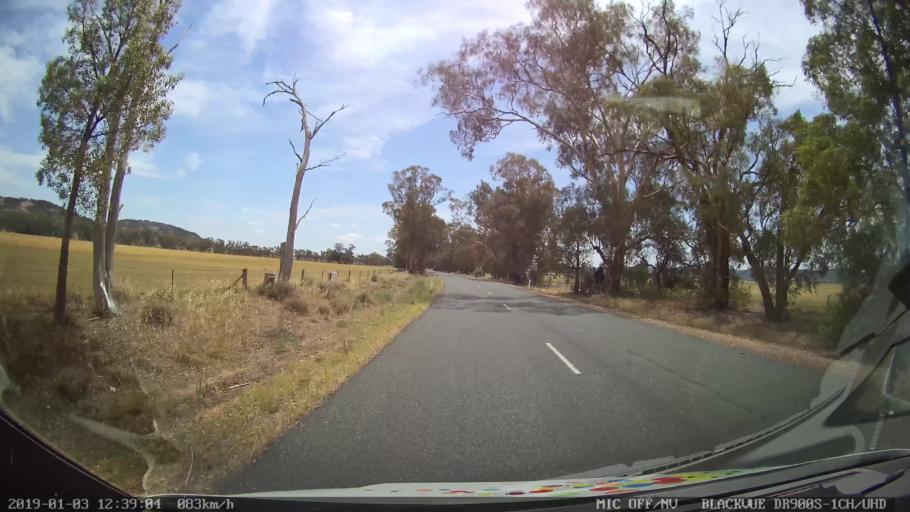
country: AU
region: New South Wales
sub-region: Weddin
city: Grenfell
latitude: -33.8283
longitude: 148.2027
